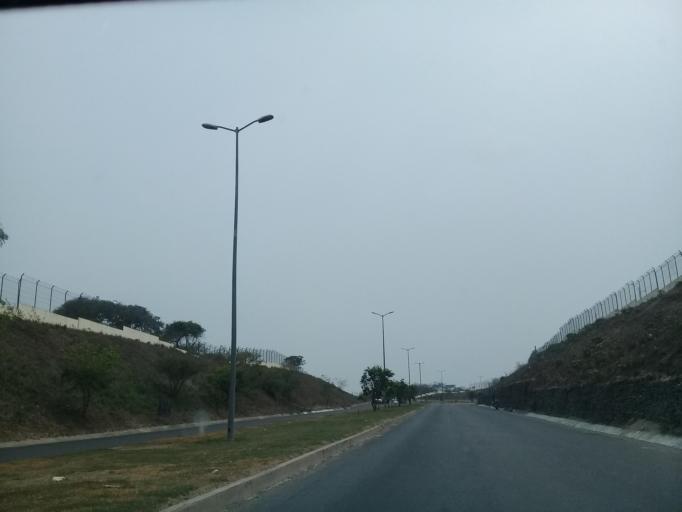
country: MX
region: Veracruz
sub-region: Veracruz
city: Colonia el Renacimiento
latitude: 19.2234
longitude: -96.2203
